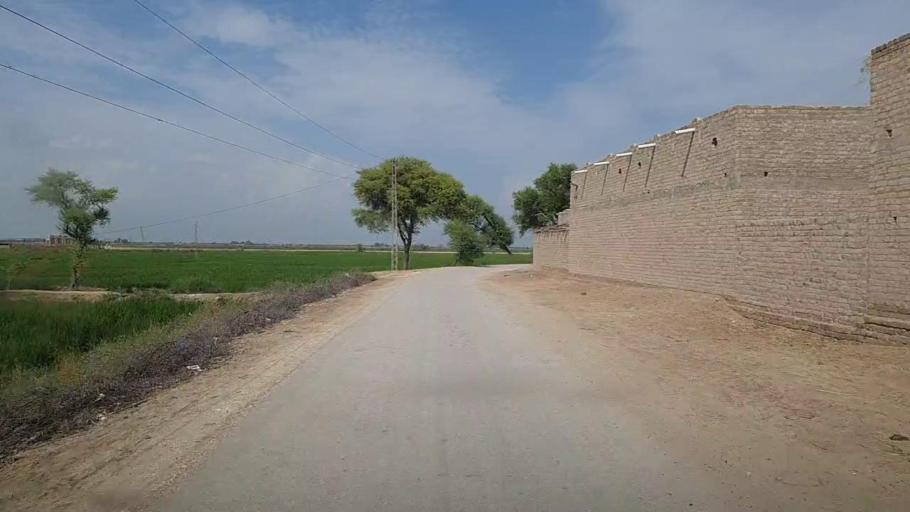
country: PK
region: Sindh
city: Thul
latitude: 28.2726
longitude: 68.8209
